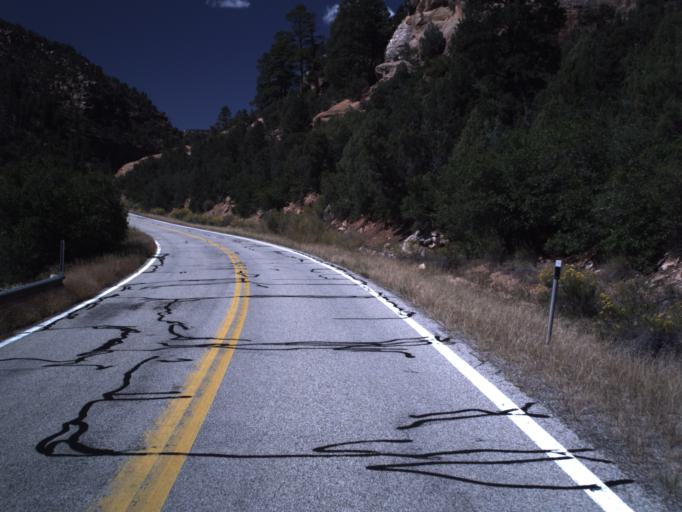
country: US
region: Utah
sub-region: San Juan County
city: Monticello
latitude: 38.3278
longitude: -109.0700
